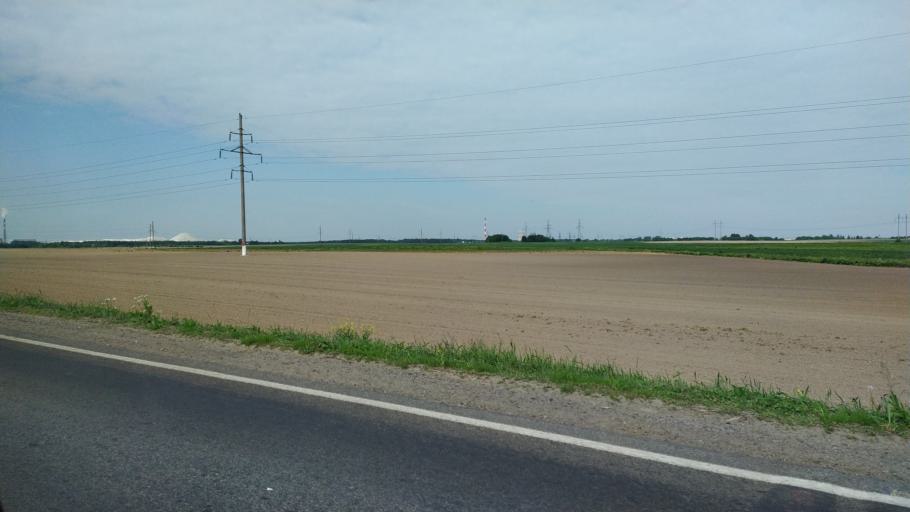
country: BY
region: Gomel
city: Gomel
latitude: 52.4539
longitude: 30.8988
